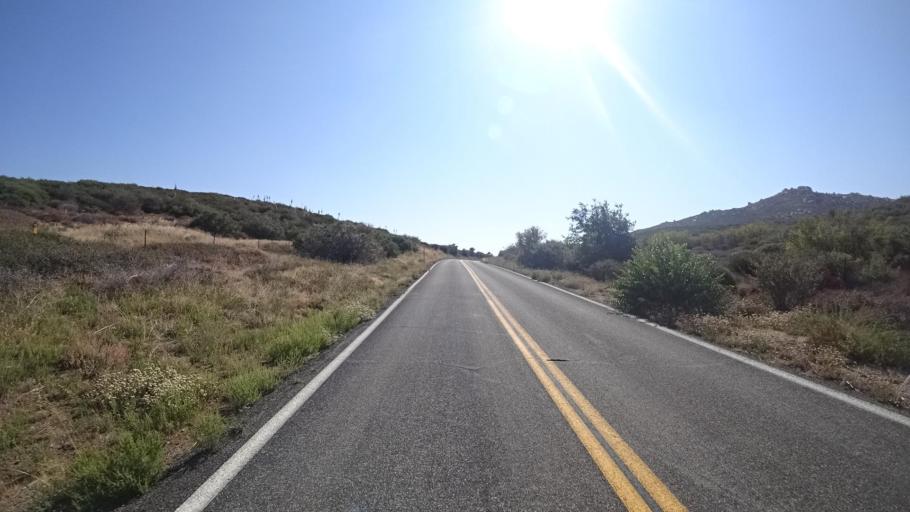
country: US
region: California
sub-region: San Diego County
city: Julian
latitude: 32.9771
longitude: -116.5225
